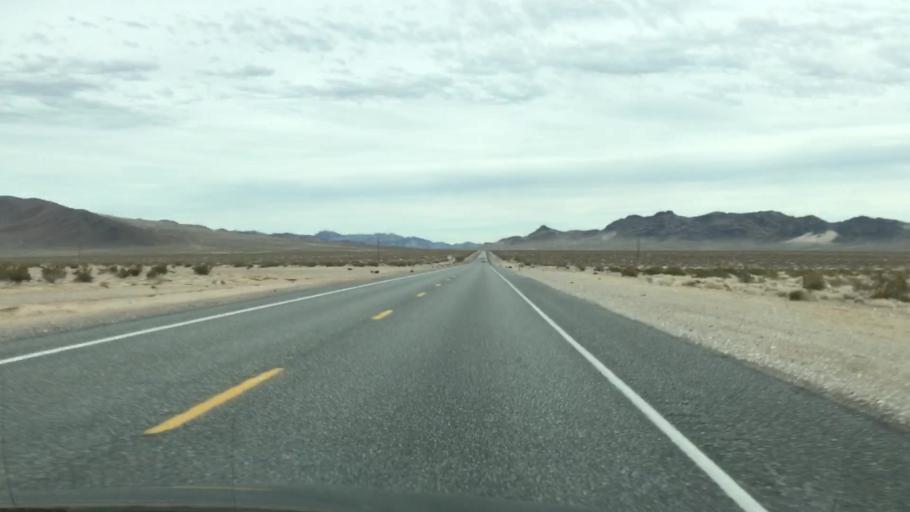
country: US
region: Nevada
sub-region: Nye County
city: Beatty
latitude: 36.6391
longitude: -116.3808
